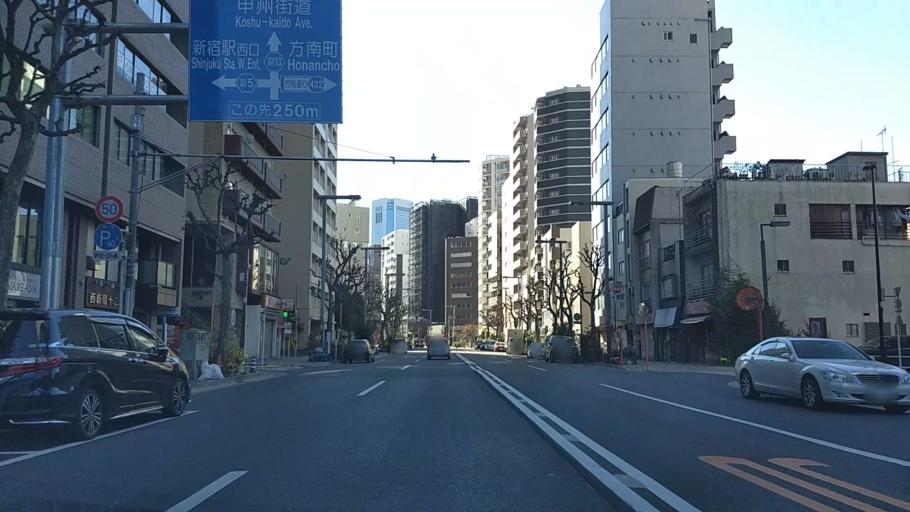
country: JP
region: Tokyo
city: Tokyo
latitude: 35.6936
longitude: 139.6871
